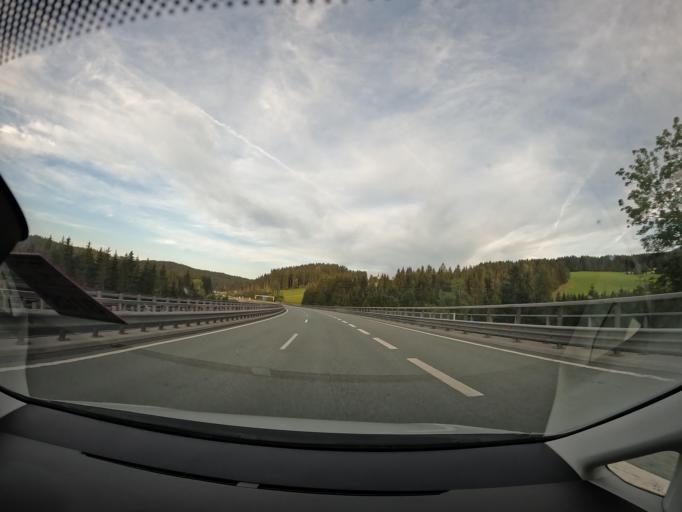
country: AT
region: Styria
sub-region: Politischer Bezirk Voitsberg
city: Modriach
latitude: 46.9557
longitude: 15.0459
